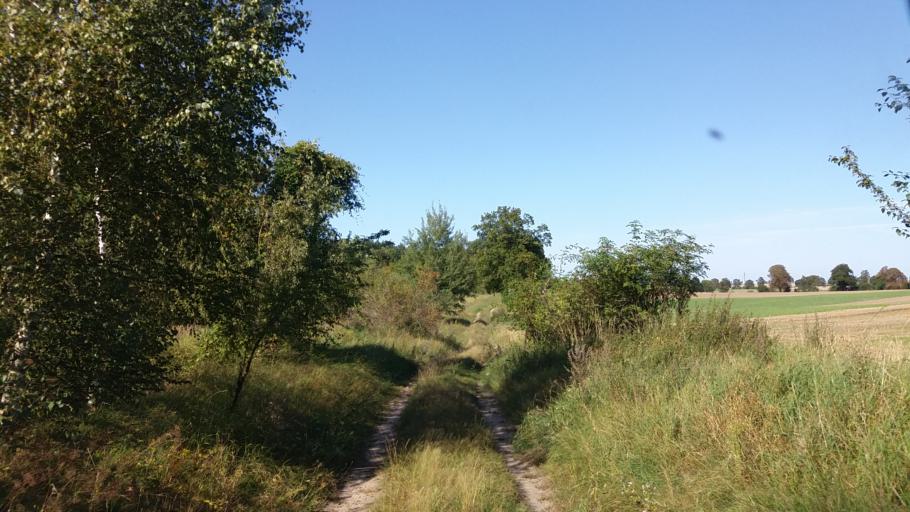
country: PL
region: West Pomeranian Voivodeship
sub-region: Powiat choszczenski
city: Krzecin
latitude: 53.1313
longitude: 15.5030
